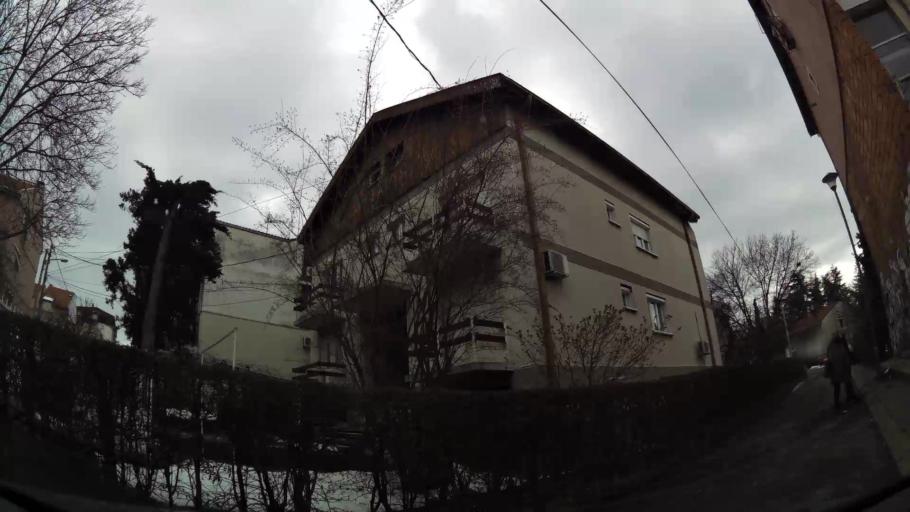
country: RS
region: Central Serbia
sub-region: Belgrade
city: Rakovica
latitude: 44.7489
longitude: 20.4059
